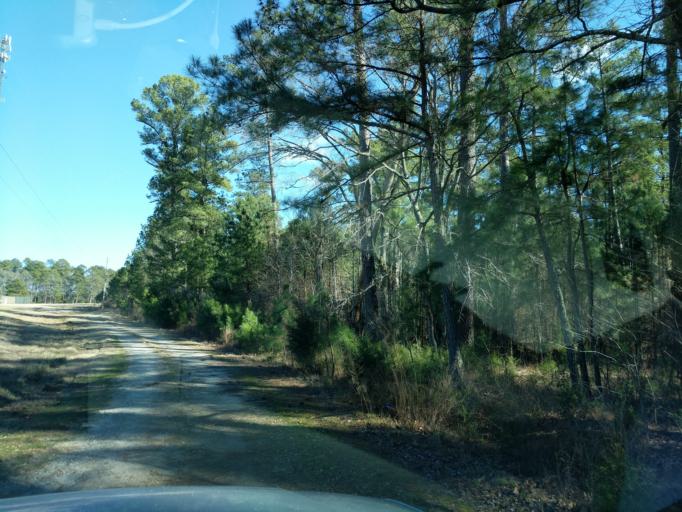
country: US
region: South Carolina
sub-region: Edgefield County
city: Edgefield
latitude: 33.9308
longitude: -82.0471
